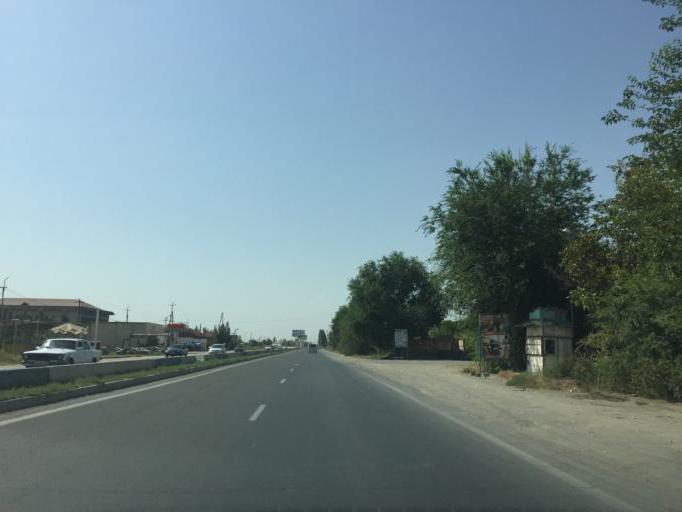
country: AM
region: Ararat
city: Artashat
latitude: 39.9513
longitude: 44.5416
